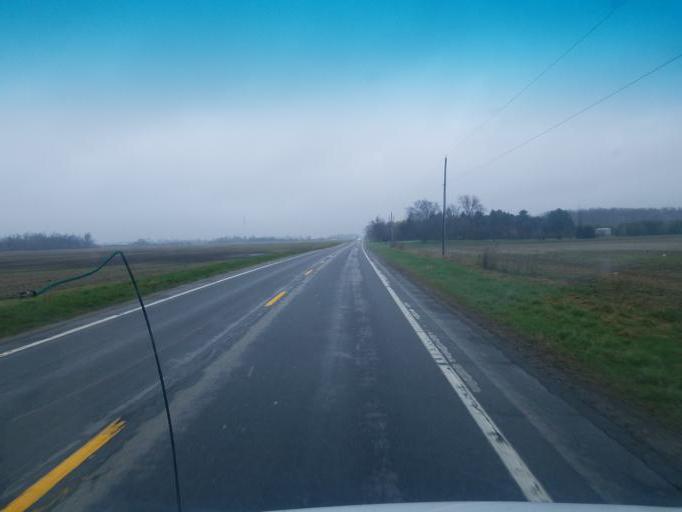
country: US
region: Ohio
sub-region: Wood County
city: Weston
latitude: 41.3724
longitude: -83.7664
